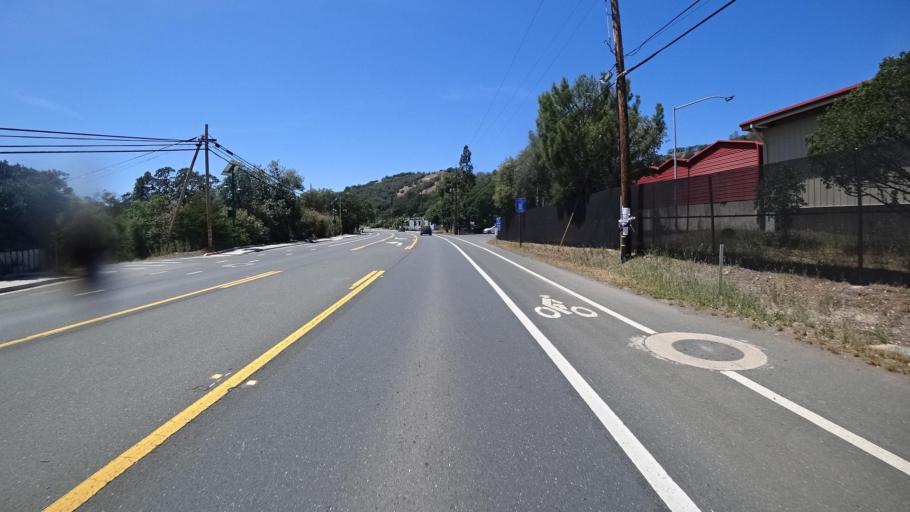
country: US
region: California
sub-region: Lake County
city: Clearlake Oaks
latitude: 39.0277
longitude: -122.6655
